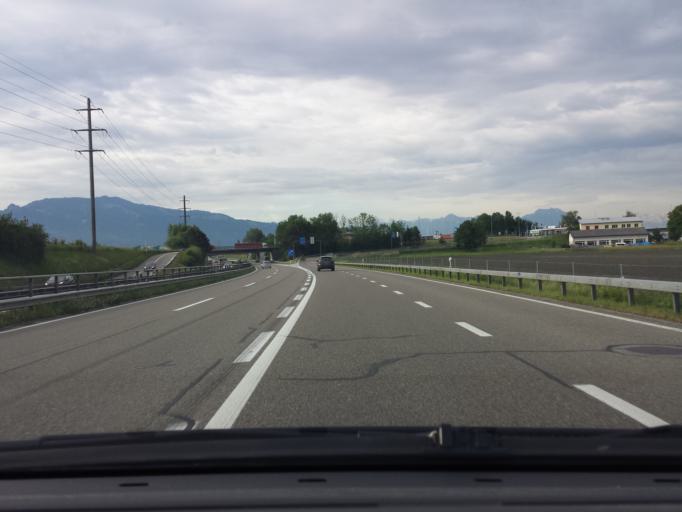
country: CH
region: Saint Gallen
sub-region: Wahlkreis Rheintal
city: Au
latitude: 47.4335
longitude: 9.6419
